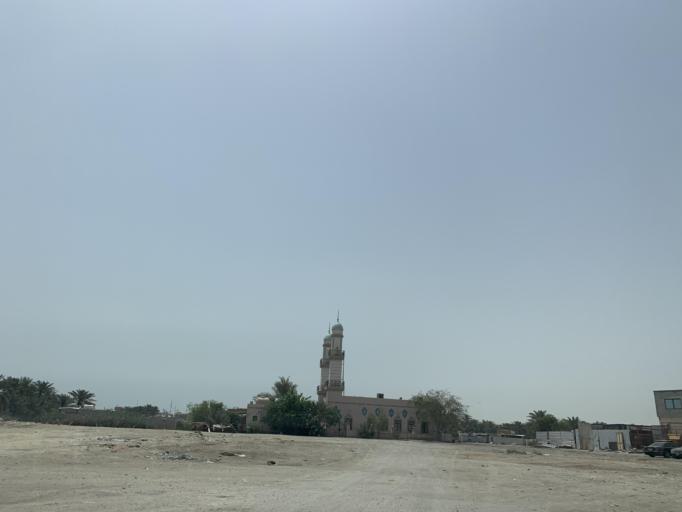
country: BH
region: Northern
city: Sitrah
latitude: 26.1383
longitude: 50.5917
